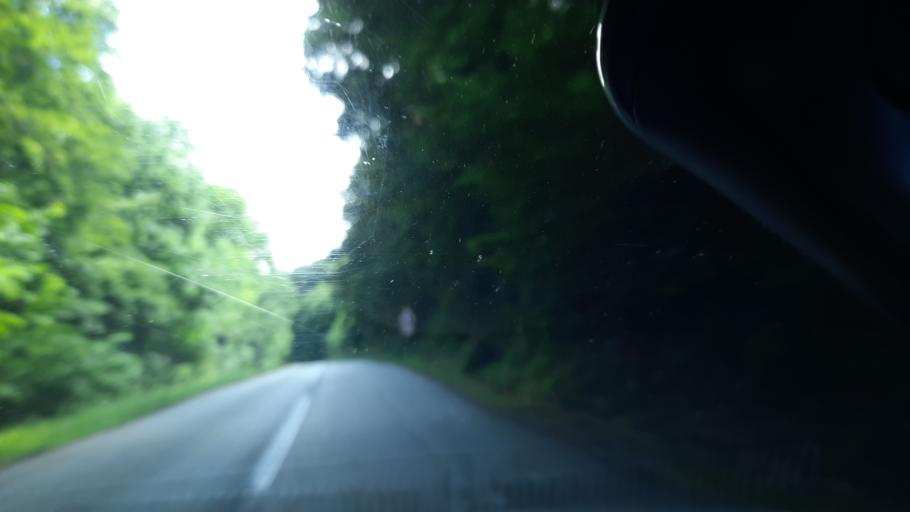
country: RS
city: Glozan
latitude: 45.1407
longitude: 19.5795
